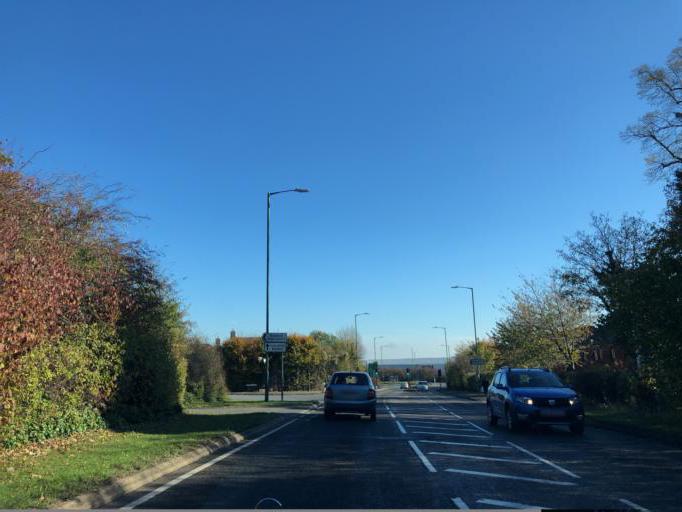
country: GB
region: England
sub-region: Warwickshire
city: Southam
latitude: 52.2491
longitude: -1.4004
